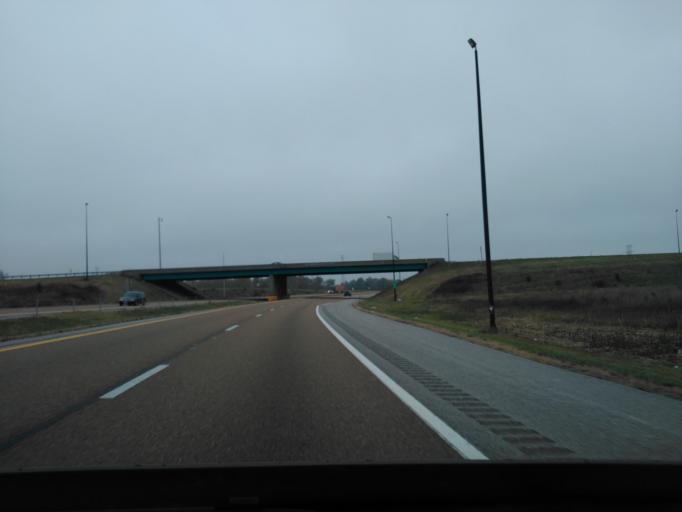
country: US
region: Illinois
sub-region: Madison County
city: Troy
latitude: 38.7197
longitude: -89.9168
